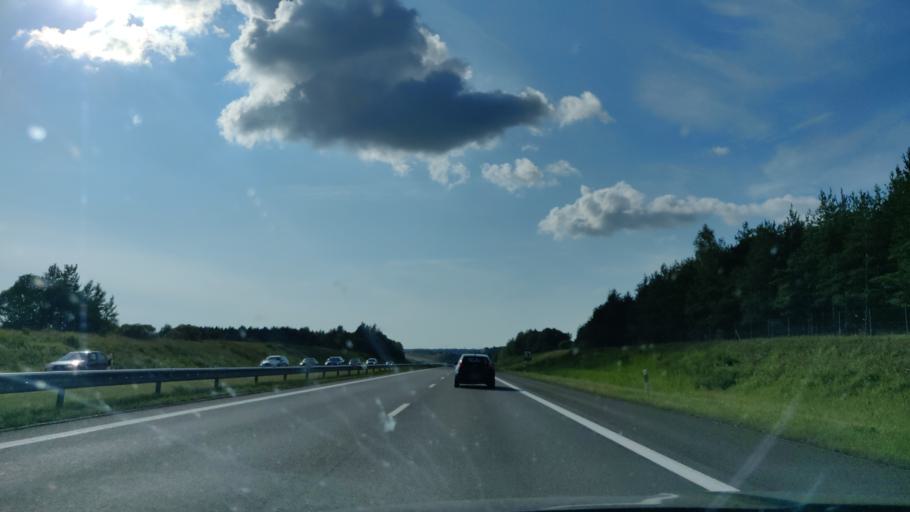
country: LT
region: Klaipedos apskritis
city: Gargzdai
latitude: 55.7229
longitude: 21.4297
